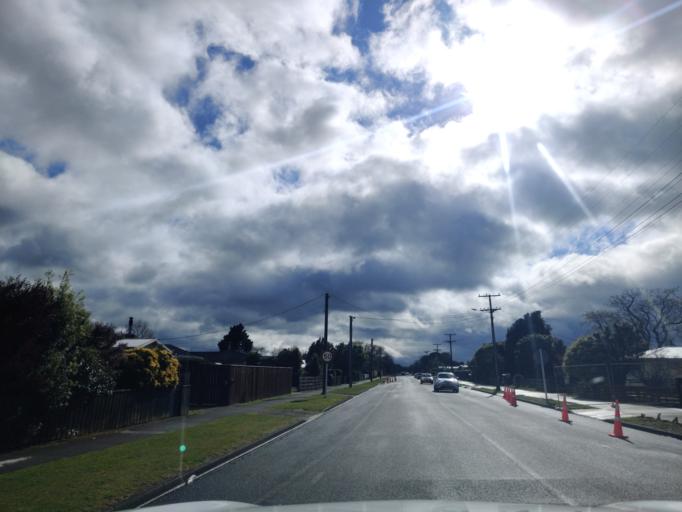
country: NZ
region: Manawatu-Wanganui
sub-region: Palmerston North City
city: Palmerston North
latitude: -40.2876
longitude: 175.7587
